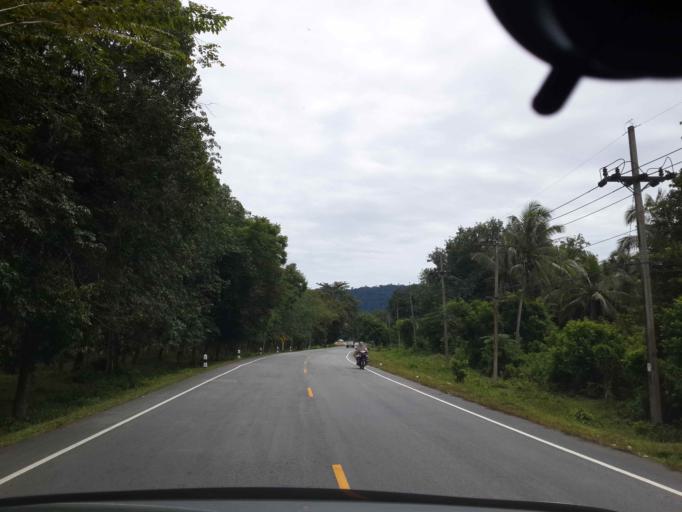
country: TH
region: Narathiwat
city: Rueso
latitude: 6.3625
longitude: 101.5915
